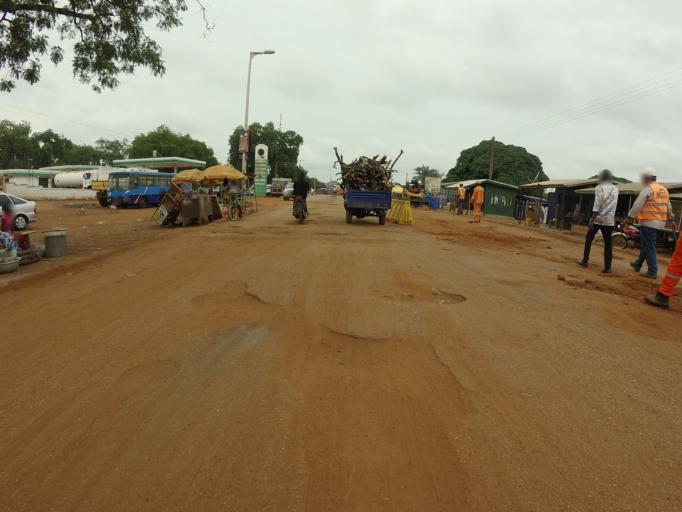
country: GH
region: Northern
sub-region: Yendi
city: Yendi
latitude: 9.4465
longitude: -0.0070
